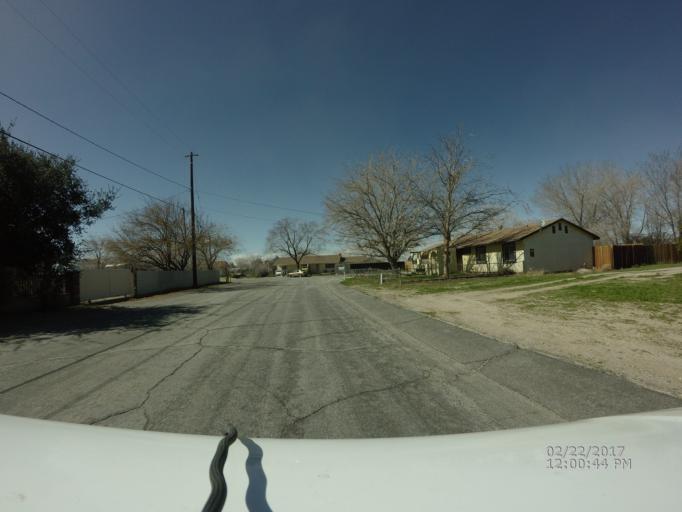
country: US
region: California
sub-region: Los Angeles County
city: Lake Los Angeles
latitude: 34.6228
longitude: -117.8341
